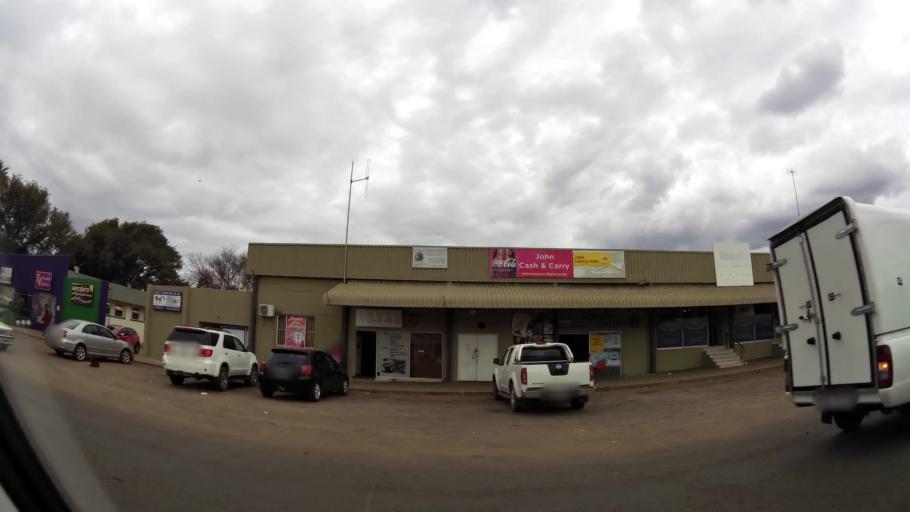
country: ZA
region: Limpopo
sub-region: Waterberg District Municipality
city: Modimolle
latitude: -24.7043
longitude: 28.4105
